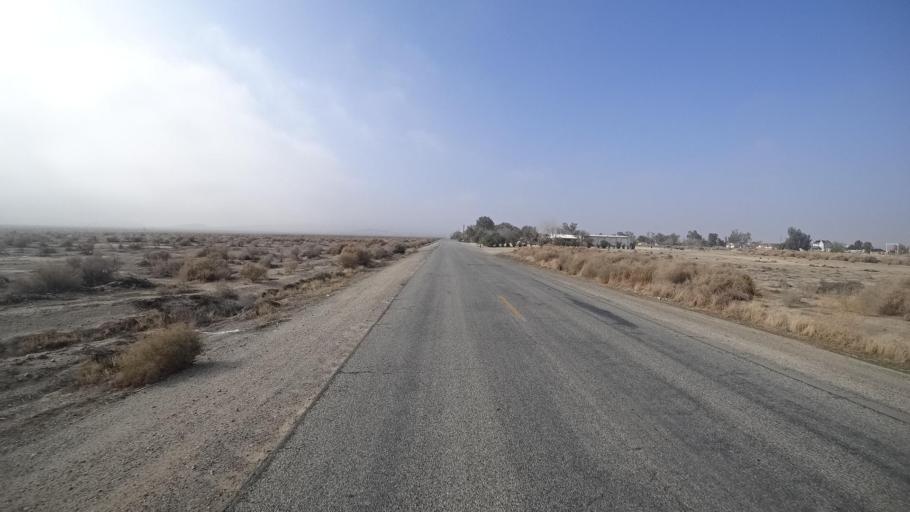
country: US
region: California
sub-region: Kern County
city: Ford City
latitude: 35.2096
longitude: -119.4194
